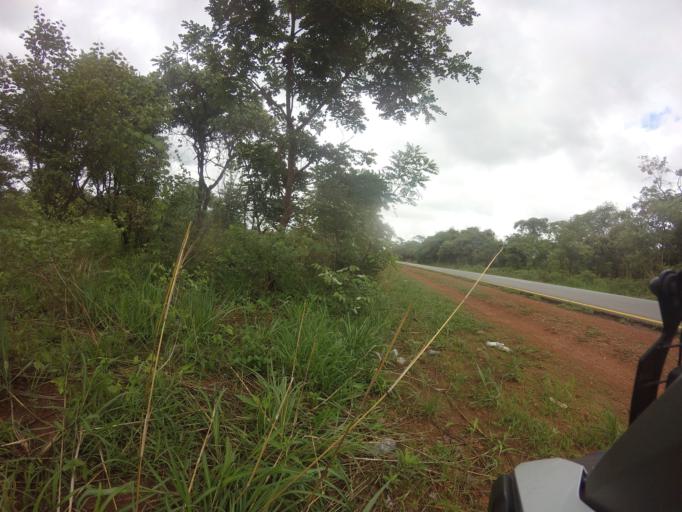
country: ZM
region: Central
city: Mumbwa
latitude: -15.1169
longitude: 27.1871
